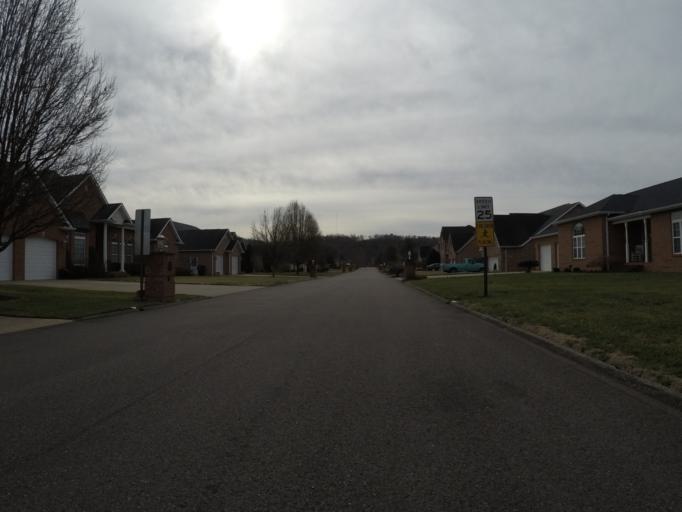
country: US
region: West Virginia
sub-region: Cabell County
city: Pea Ridge
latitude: 38.4461
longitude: -82.3486
